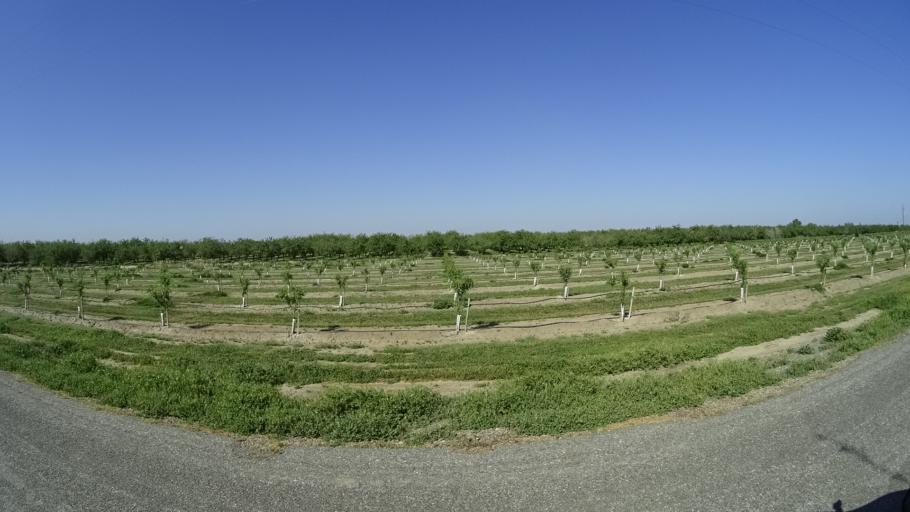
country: US
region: California
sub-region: Glenn County
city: Hamilton City
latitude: 39.6193
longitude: -122.0274
